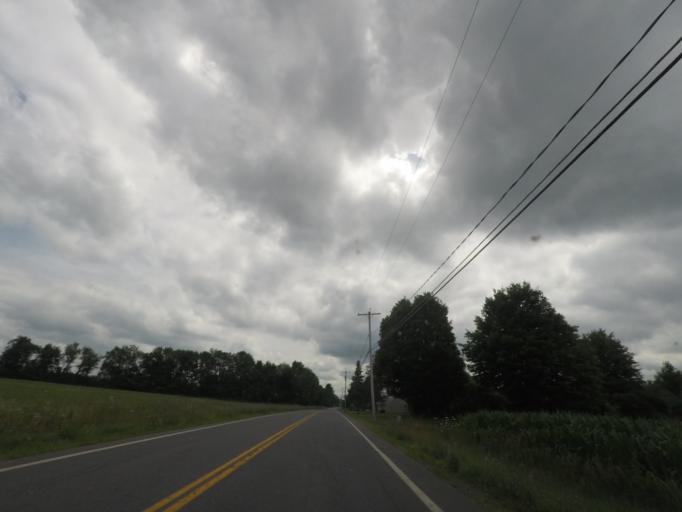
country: US
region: New York
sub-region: Saratoga County
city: Stillwater
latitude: 43.0180
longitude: -73.6918
